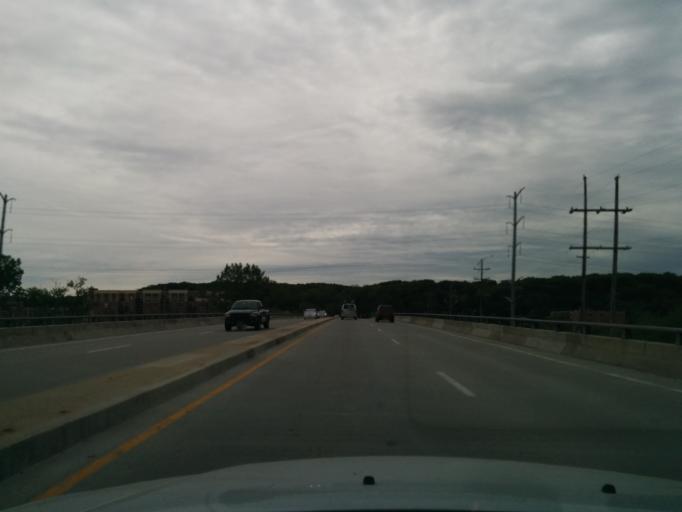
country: US
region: Illinois
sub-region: Cook County
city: Willow Springs
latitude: 41.7346
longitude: -87.8804
